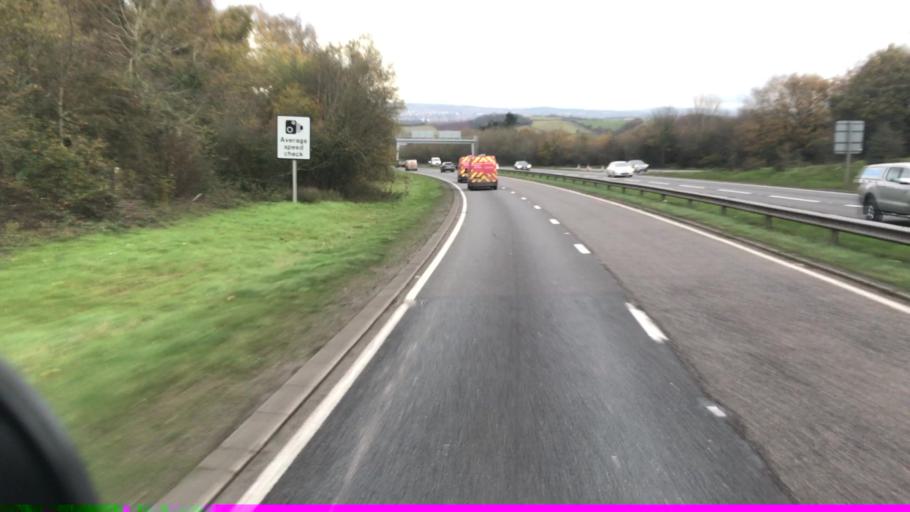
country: GB
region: England
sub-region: Devon
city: Exminster
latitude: 50.6494
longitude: -3.5420
